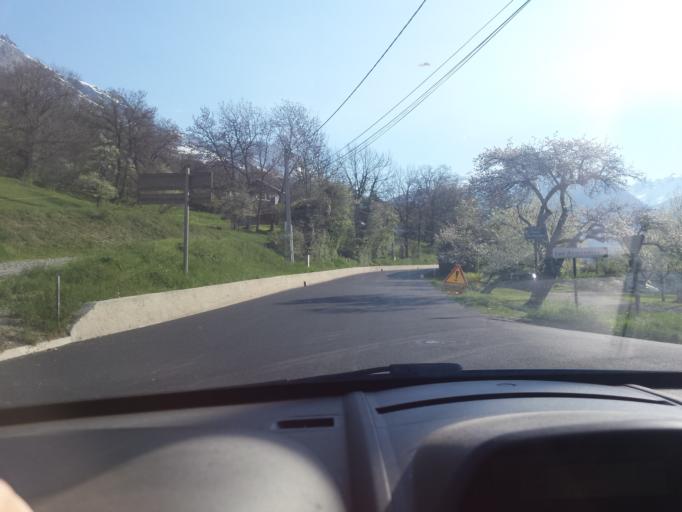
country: FR
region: Rhone-Alpes
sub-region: Departement de la Haute-Savoie
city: Passy
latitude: 45.9270
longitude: 6.7060
